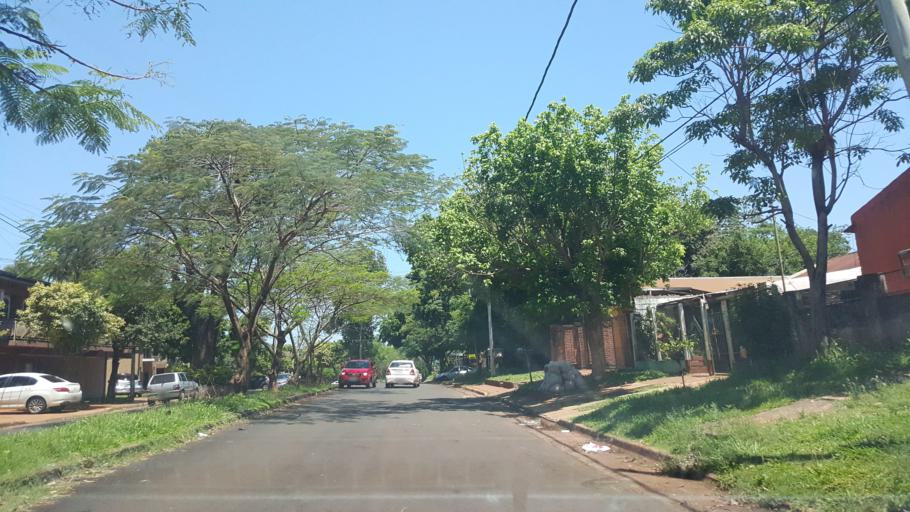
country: AR
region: Misiones
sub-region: Departamento de Capital
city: Posadas
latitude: -27.3703
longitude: -55.9208
